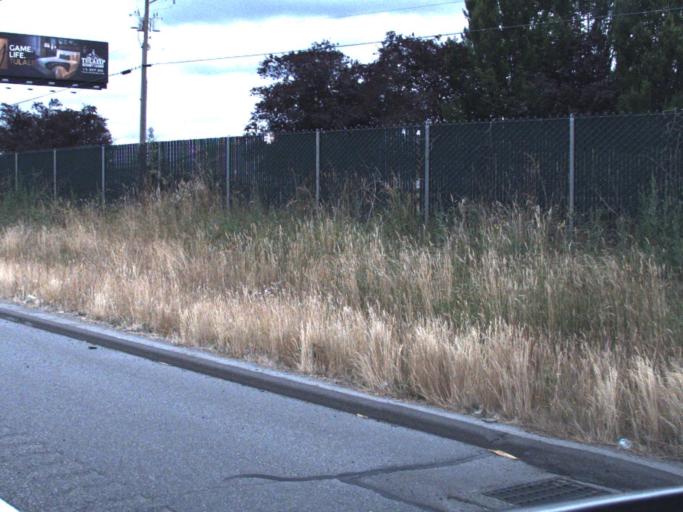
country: US
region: Washington
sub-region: Snohomish County
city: Maltby
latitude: 47.7956
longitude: -122.1285
